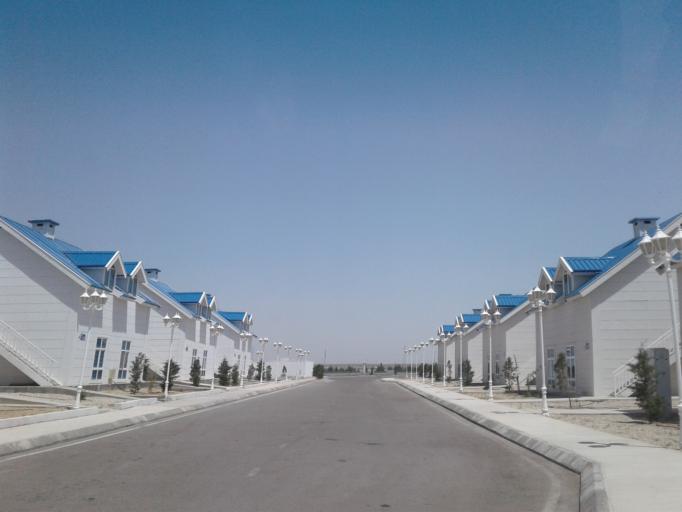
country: TM
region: Balkan
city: Turkmenbasy
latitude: 39.9871
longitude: 52.8282
